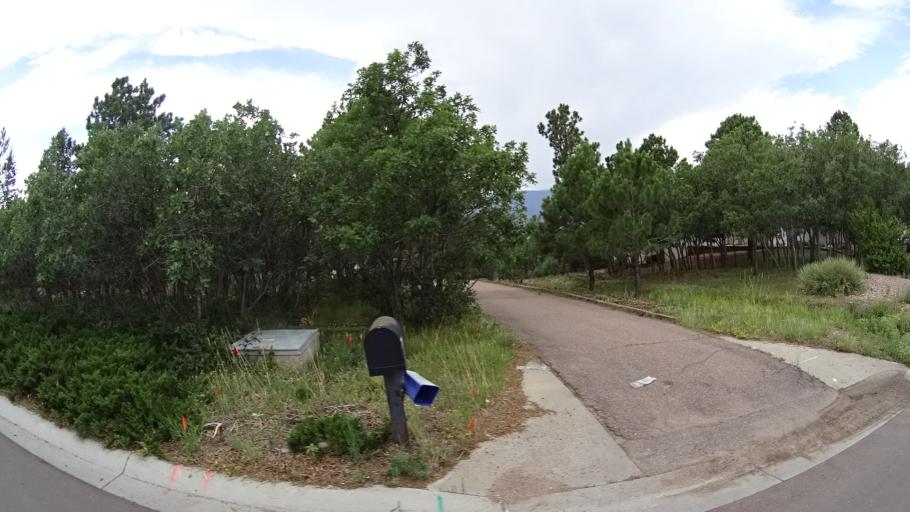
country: US
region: Colorado
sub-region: El Paso County
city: Colorado Springs
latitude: 38.9042
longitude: -104.8392
